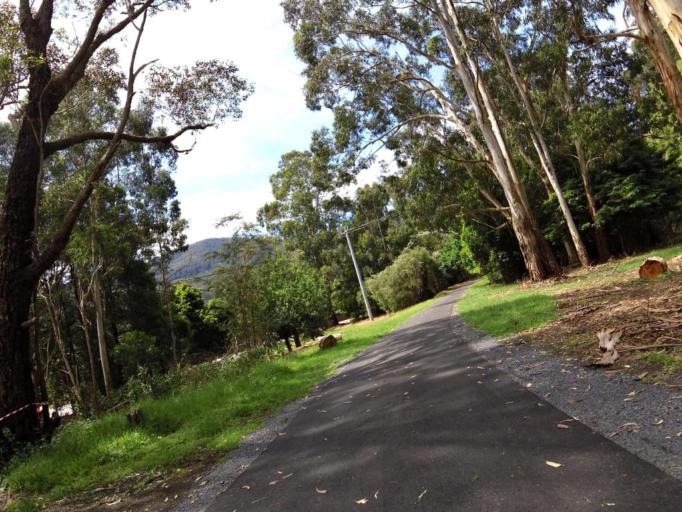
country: AU
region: Victoria
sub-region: Yarra Ranges
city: Millgrove
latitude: -37.7543
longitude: 145.6548
